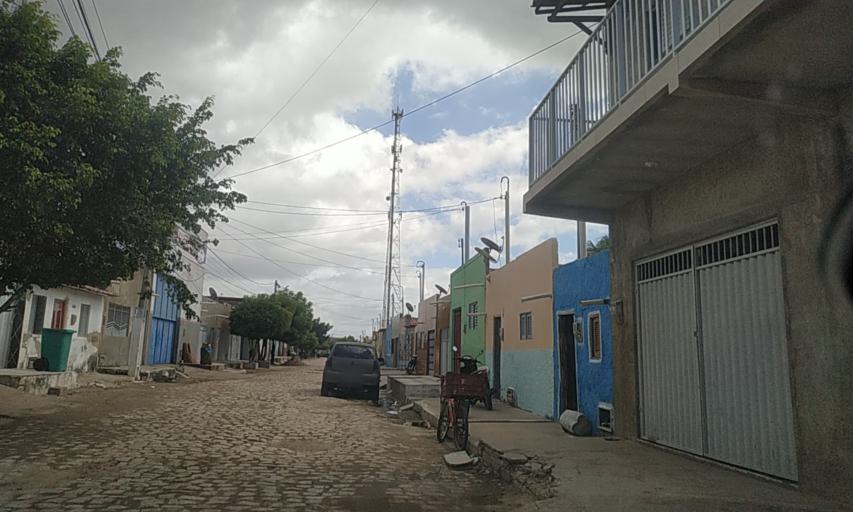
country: BR
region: Rio Grande do Norte
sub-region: Areia Branca
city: Areia Branca
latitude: -4.9517
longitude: -37.1260
